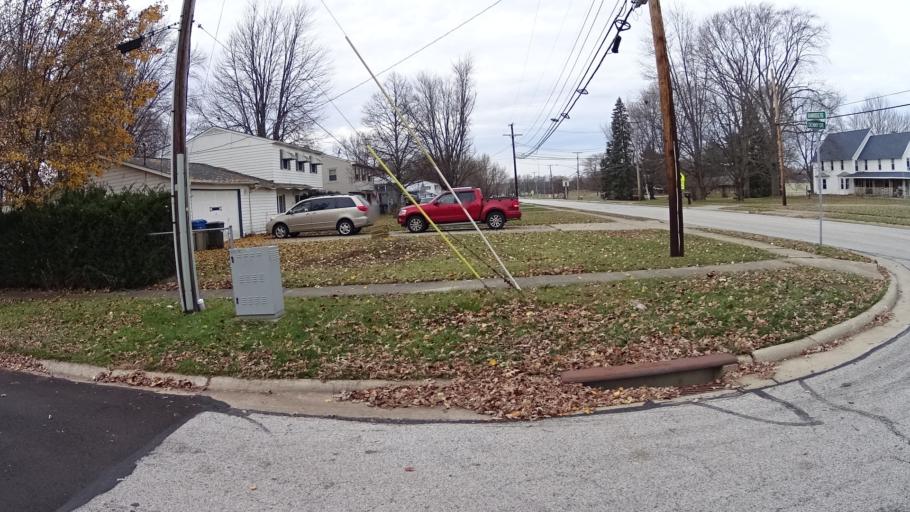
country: US
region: Ohio
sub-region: Lorain County
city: North Ridgeville
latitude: 41.3850
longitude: -81.9991
